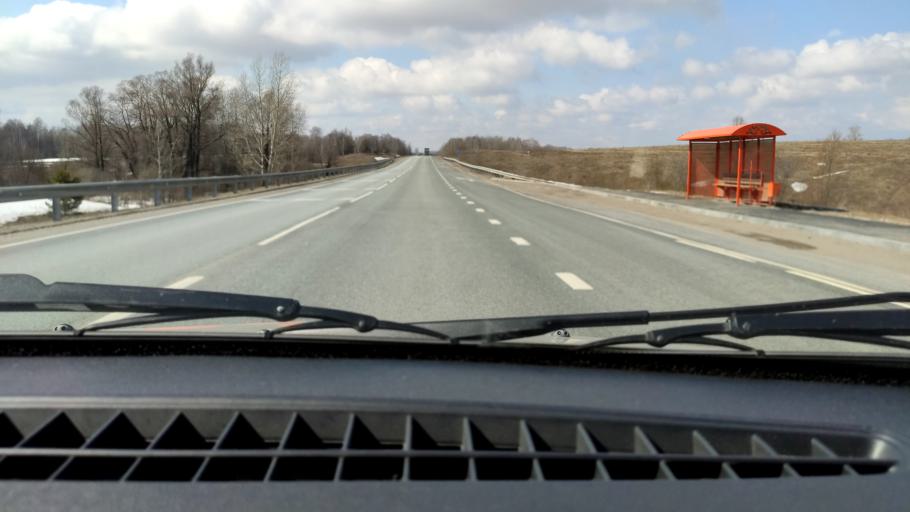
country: RU
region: Bashkortostan
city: Kudeyevskiy
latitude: 54.8172
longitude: 56.7906
